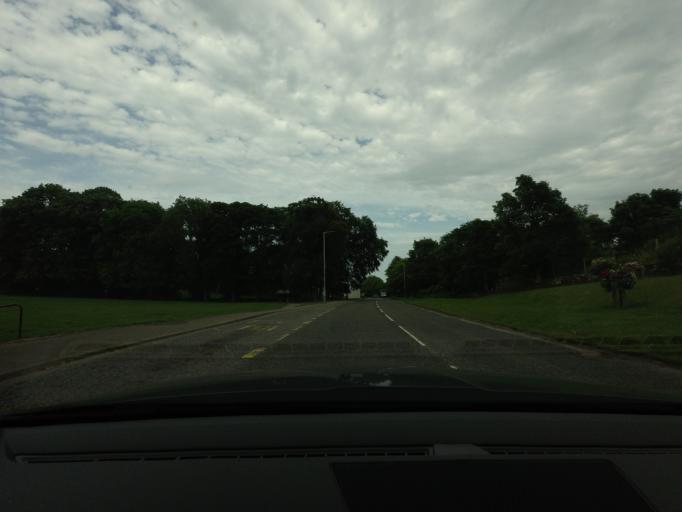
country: GB
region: Scotland
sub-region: Highland
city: Alness
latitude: 57.6940
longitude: -4.2669
